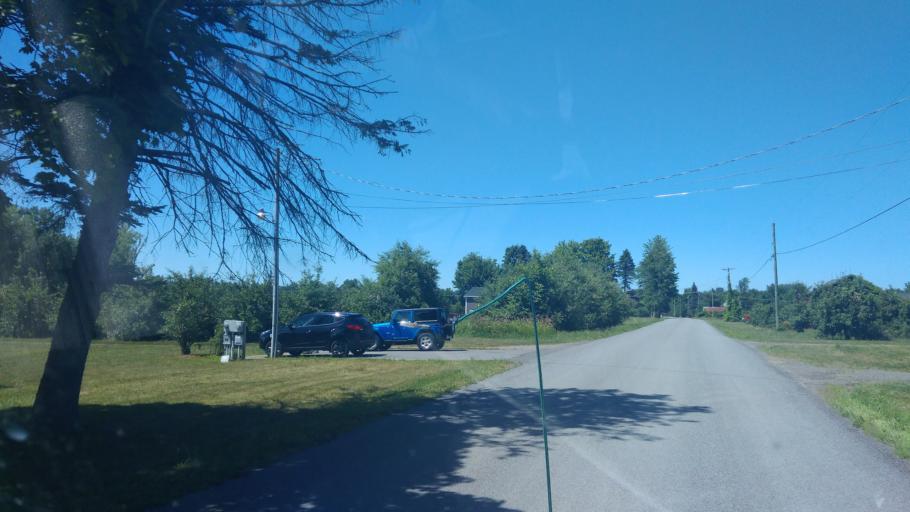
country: US
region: New York
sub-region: Wayne County
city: Sodus
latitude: 43.1731
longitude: -76.9776
